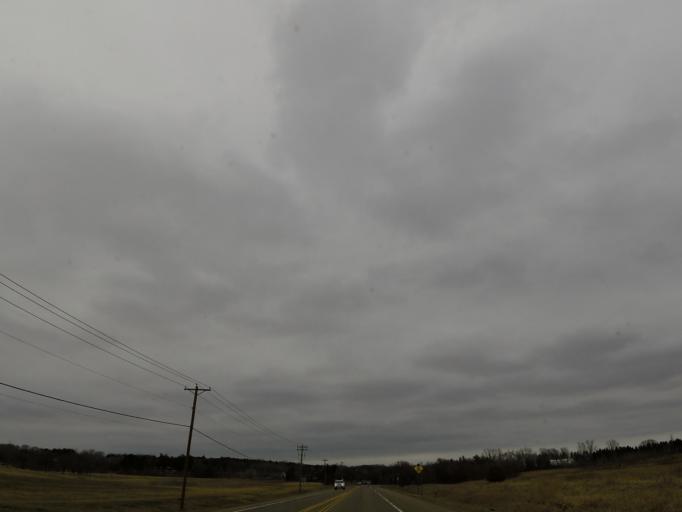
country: US
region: Minnesota
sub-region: Washington County
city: Bayport
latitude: 45.0134
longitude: -92.7964
